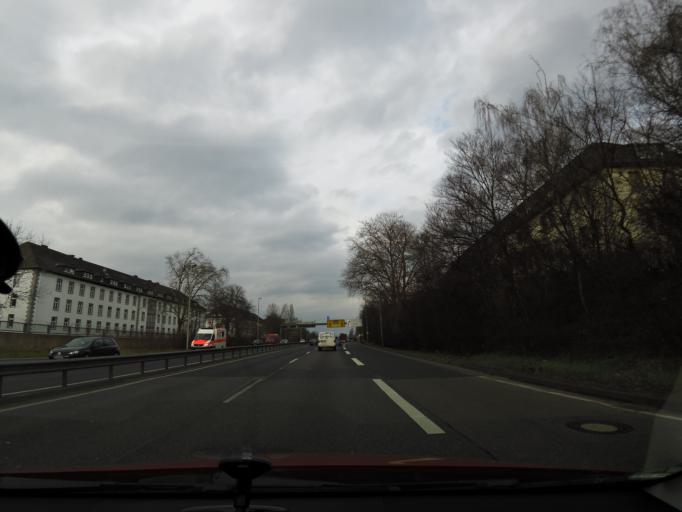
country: DE
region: Rheinland-Pfalz
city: Koblenz
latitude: 50.3712
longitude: 7.5869
